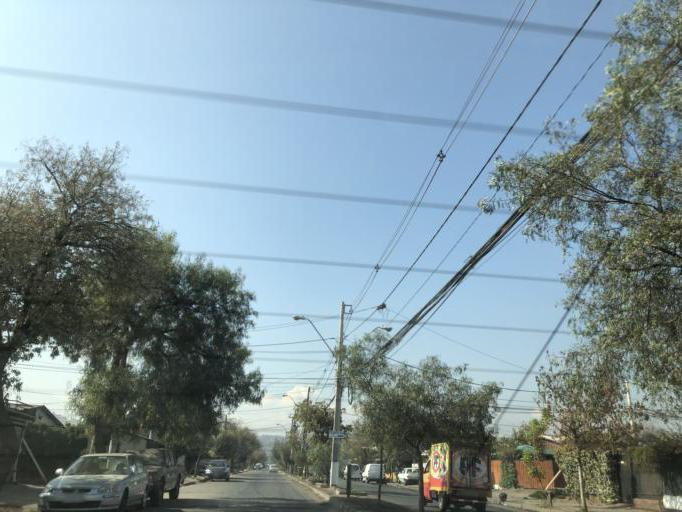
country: CL
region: Santiago Metropolitan
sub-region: Provincia de Cordillera
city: Puente Alto
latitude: -33.6043
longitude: -70.5644
